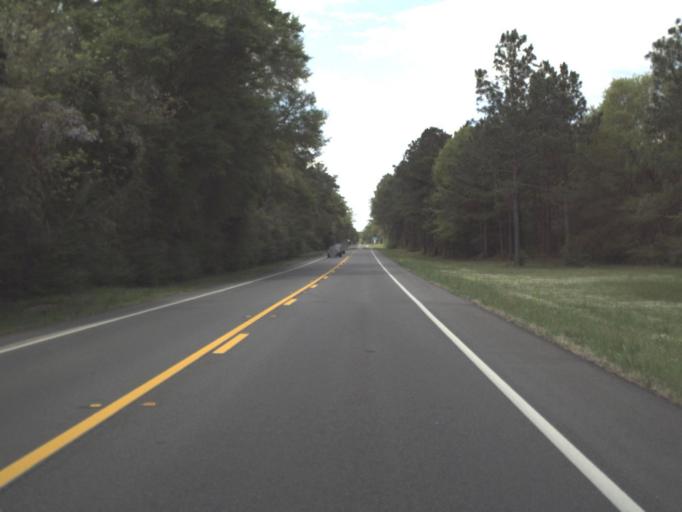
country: US
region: Florida
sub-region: Okaloosa County
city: Crestview
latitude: 30.9190
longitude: -86.4847
